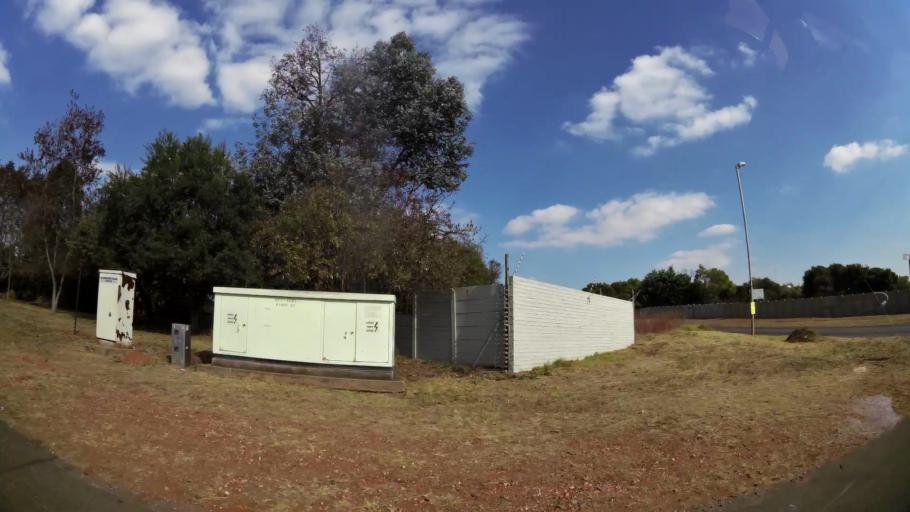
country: ZA
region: Gauteng
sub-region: West Rand District Municipality
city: Krugersdorp
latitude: -26.0483
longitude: 27.7544
